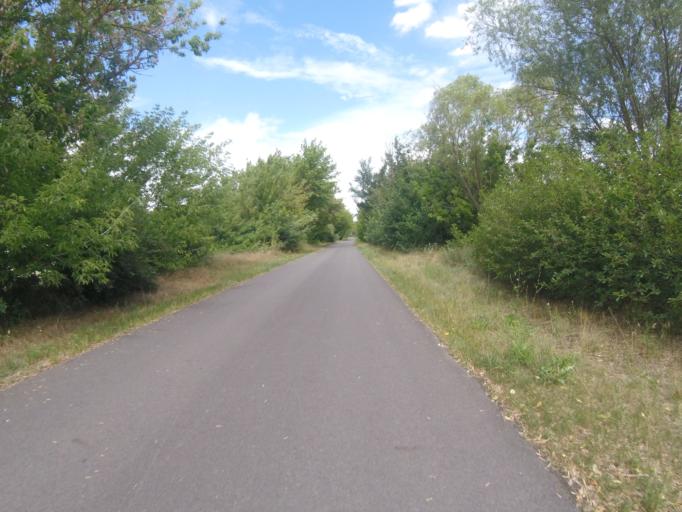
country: DE
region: Brandenburg
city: Bestensee
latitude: 52.2292
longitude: 13.7055
